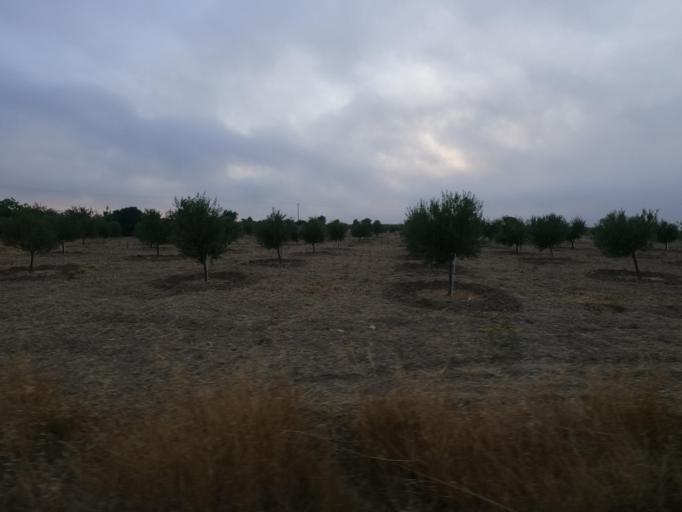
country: CY
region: Larnaka
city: Tersefanou
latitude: 34.8329
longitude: 33.5098
